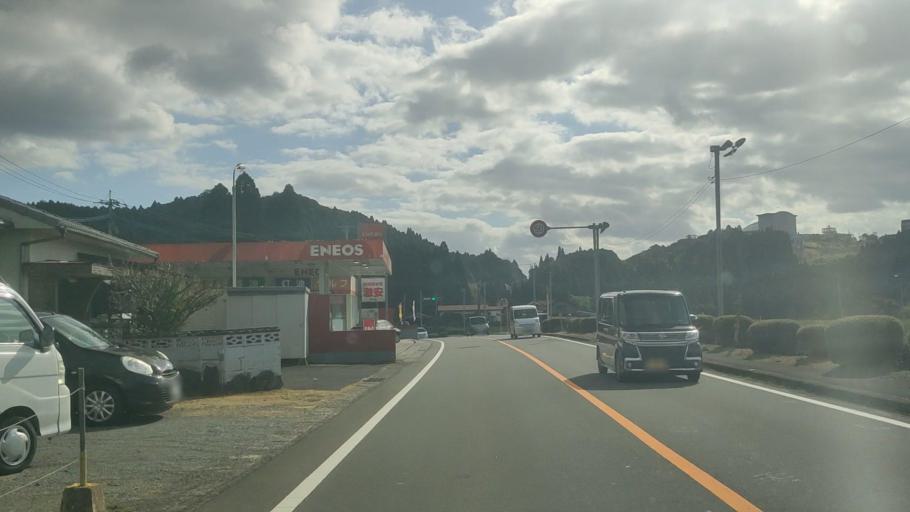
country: JP
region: Kagoshima
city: Kajiki
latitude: 31.8328
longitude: 130.6879
